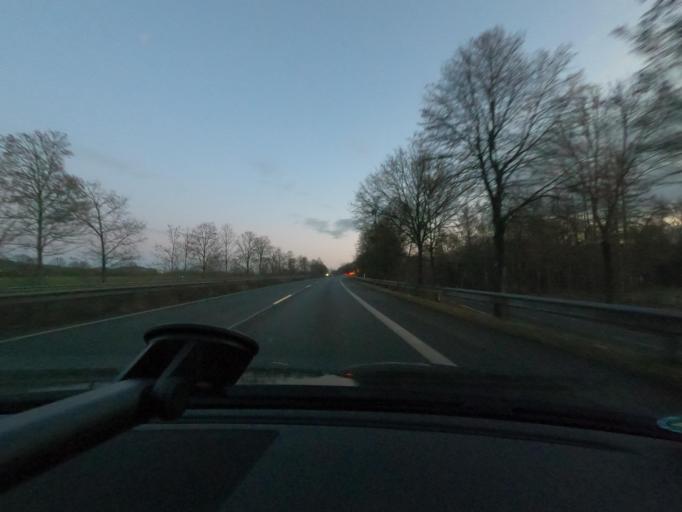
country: DE
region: Lower Saxony
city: Herzberg am Harz
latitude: 51.6681
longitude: 10.3192
